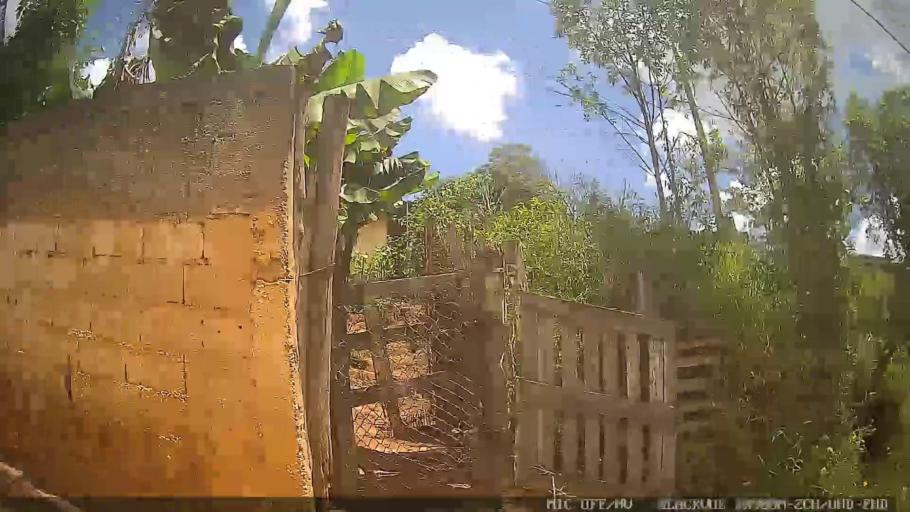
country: BR
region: Sao Paulo
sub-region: Jarinu
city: Jarinu
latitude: -23.1355
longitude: -46.6458
